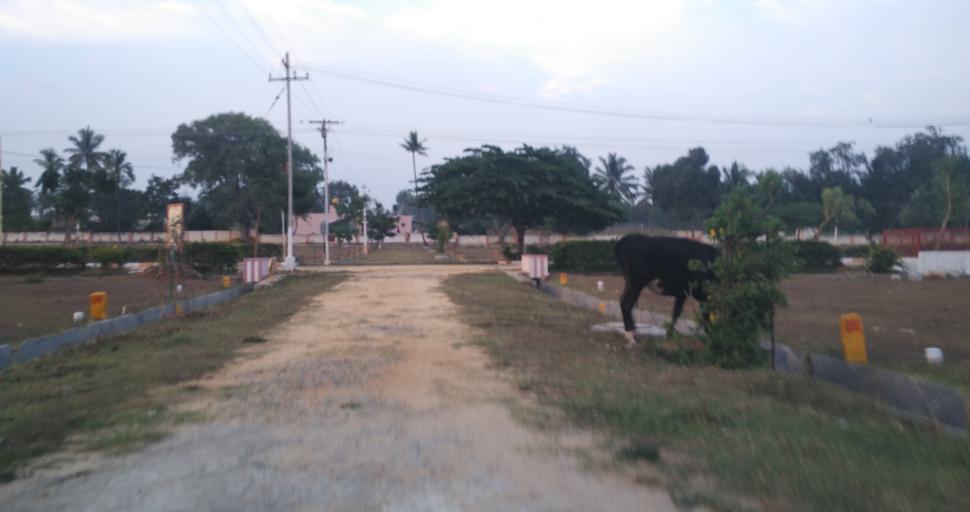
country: IN
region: Tamil Nadu
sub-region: Krishnagiri
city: Hosur
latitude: 12.6699
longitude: 77.8281
